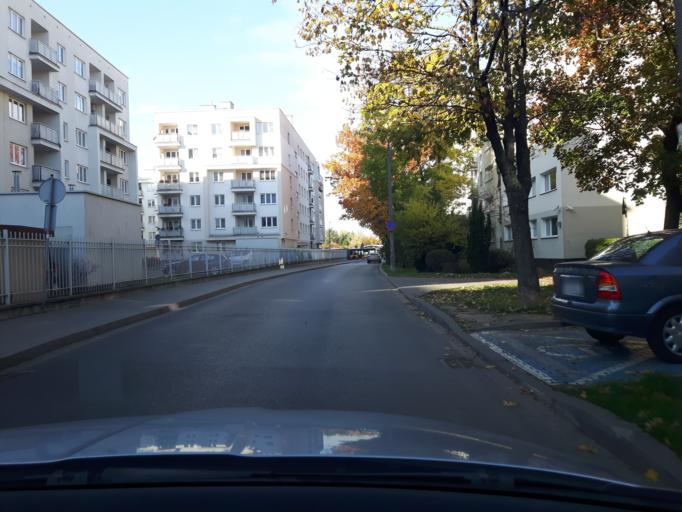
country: PL
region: Masovian Voivodeship
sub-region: Warszawa
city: Bemowo
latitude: 52.2329
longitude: 20.9336
